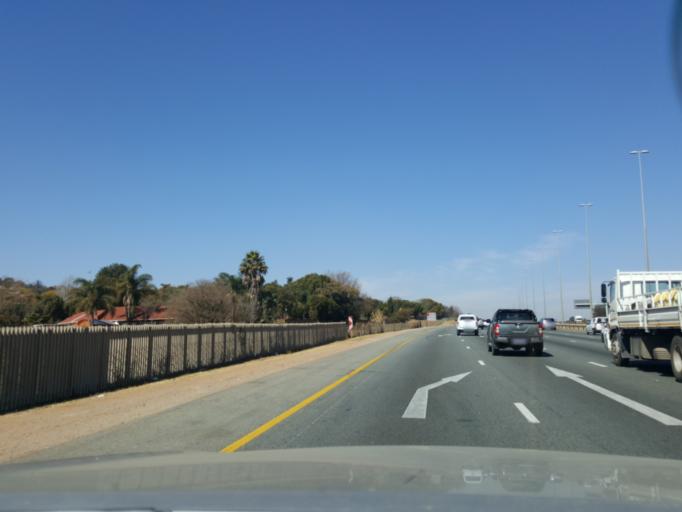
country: ZA
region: Gauteng
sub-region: City of Tshwane Metropolitan Municipality
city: Centurion
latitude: -25.8365
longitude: 28.2478
